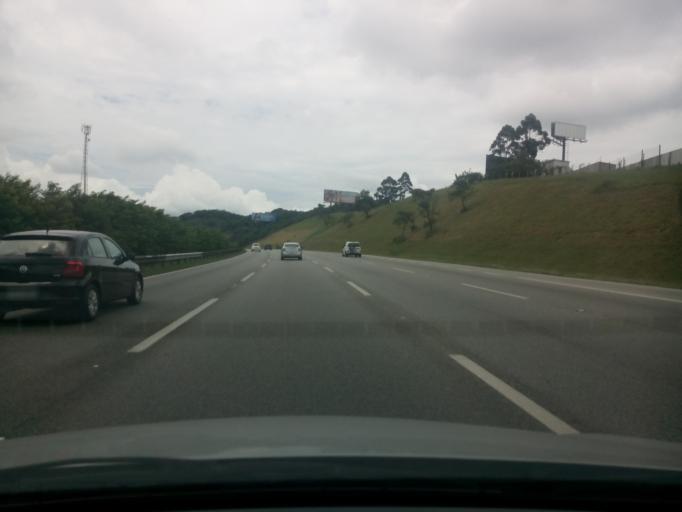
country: BR
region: Sao Paulo
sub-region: Diadema
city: Diadema
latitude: -23.7243
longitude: -46.6071
